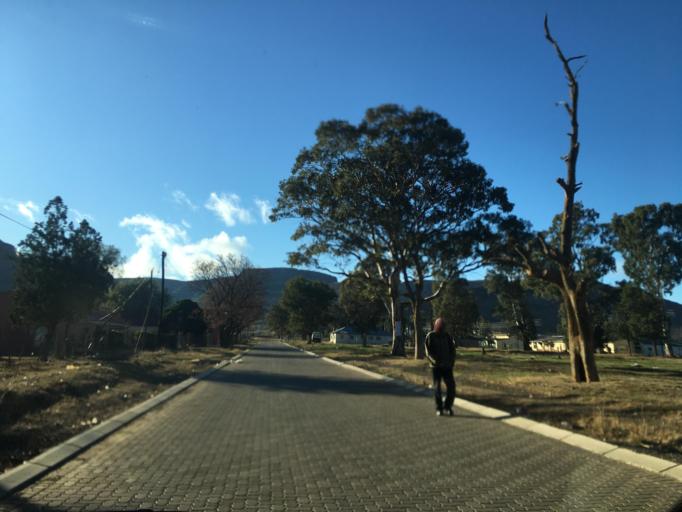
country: ZA
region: Eastern Cape
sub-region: Chris Hani District Municipality
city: Cala
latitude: -31.5266
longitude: 27.7000
